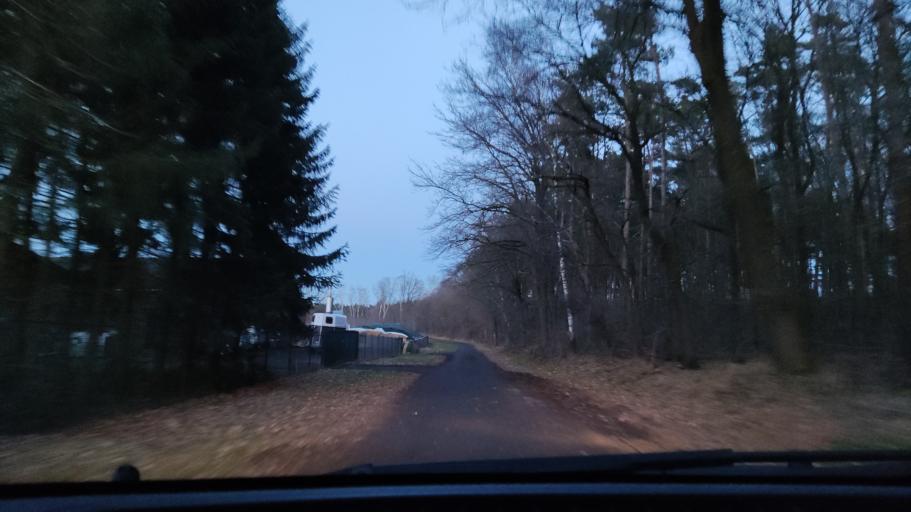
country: DE
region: Lower Saxony
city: Thomasburg
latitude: 53.1973
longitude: 10.6485
